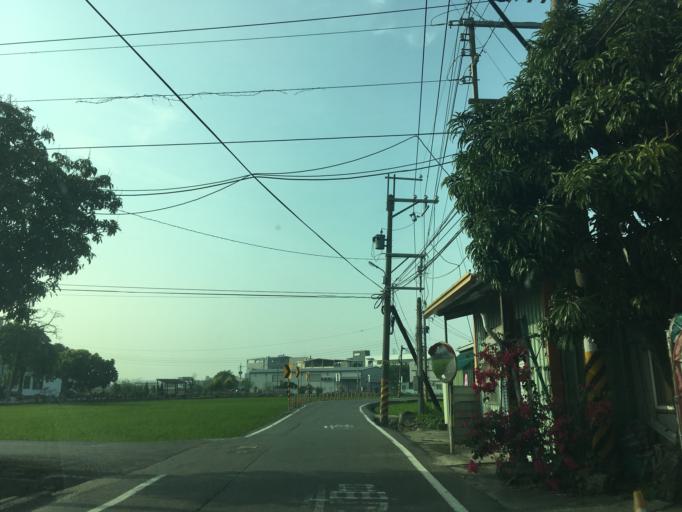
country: TW
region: Taiwan
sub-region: Taichung City
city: Taichung
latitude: 24.0556
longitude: 120.6809
